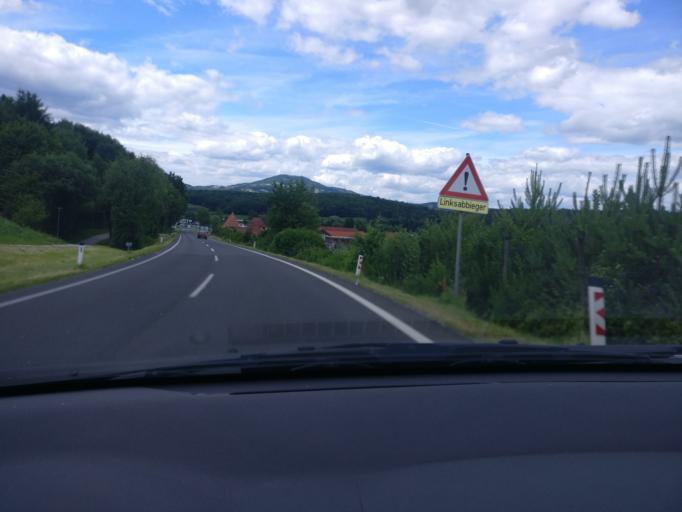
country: AT
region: Styria
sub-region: Politischer Bezirk Weiz
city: Oberrettenbach
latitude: 47.1455
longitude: 15.7714
